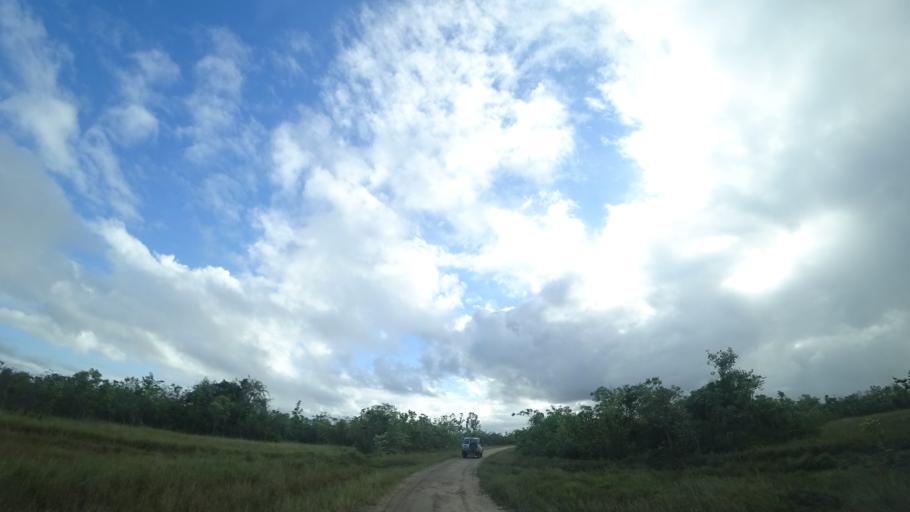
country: MZ
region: Sofala
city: Beira
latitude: -19.6671
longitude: 35.0582
